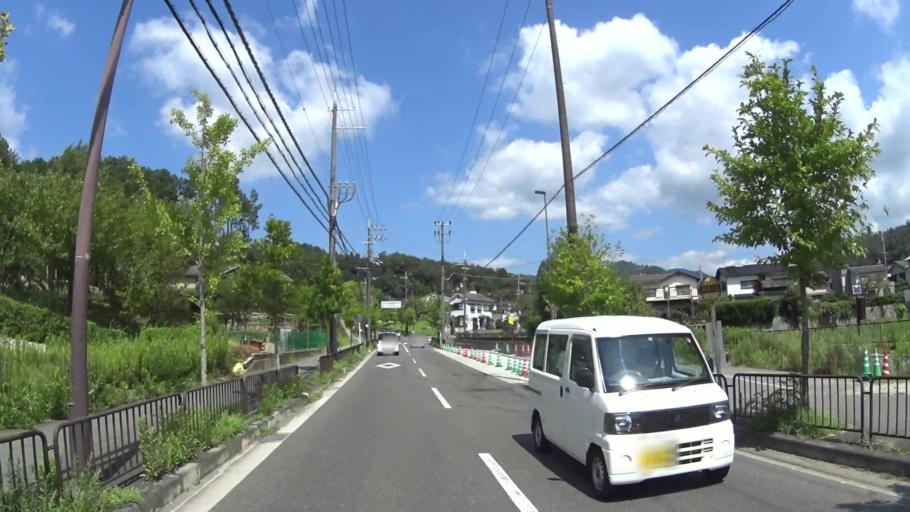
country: JP
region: Kyoto
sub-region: Kyoto-shi
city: Kamigyo-ku
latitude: 35.0731
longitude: 135.7660
